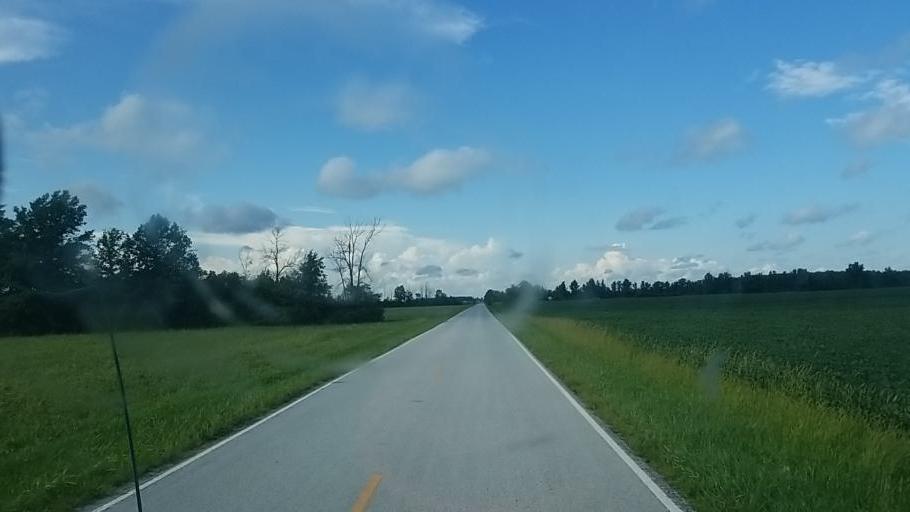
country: US
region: Ohio
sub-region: Hardin County
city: Forest
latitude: 40.7478
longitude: -83.4966
